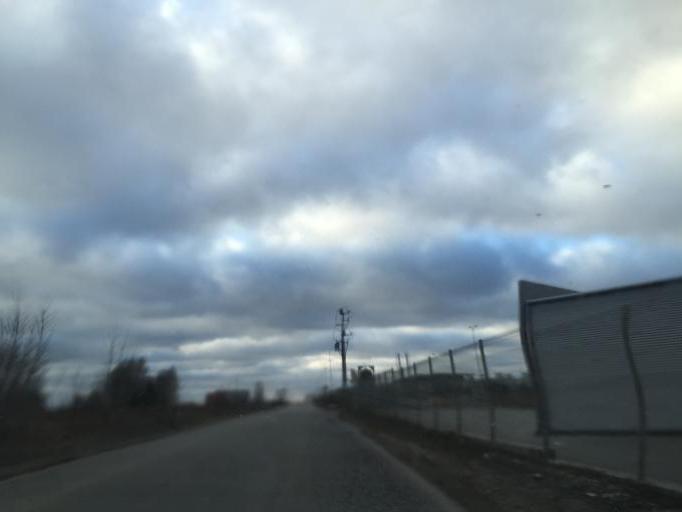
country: PL
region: Pomeranian Voivodeship
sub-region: Gdynia
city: Wielki Kack
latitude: 54.4119
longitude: 18.4806
